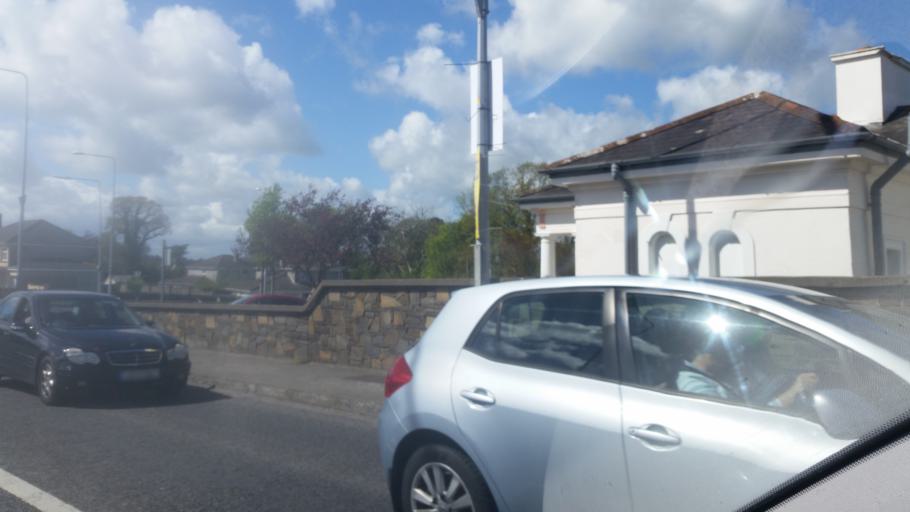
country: IE
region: Munster
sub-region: Waterford
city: Waterford
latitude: 52.2473
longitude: -7.0830
